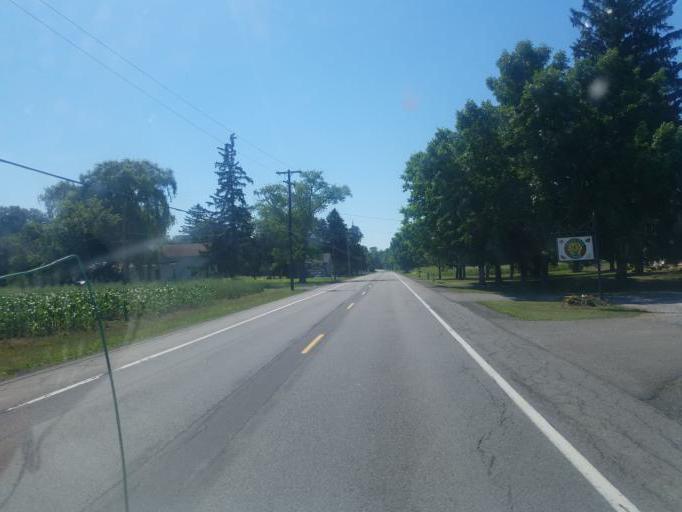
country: US
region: New York
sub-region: Ontario County
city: Phelps
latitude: 42.9497
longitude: -77.0244
